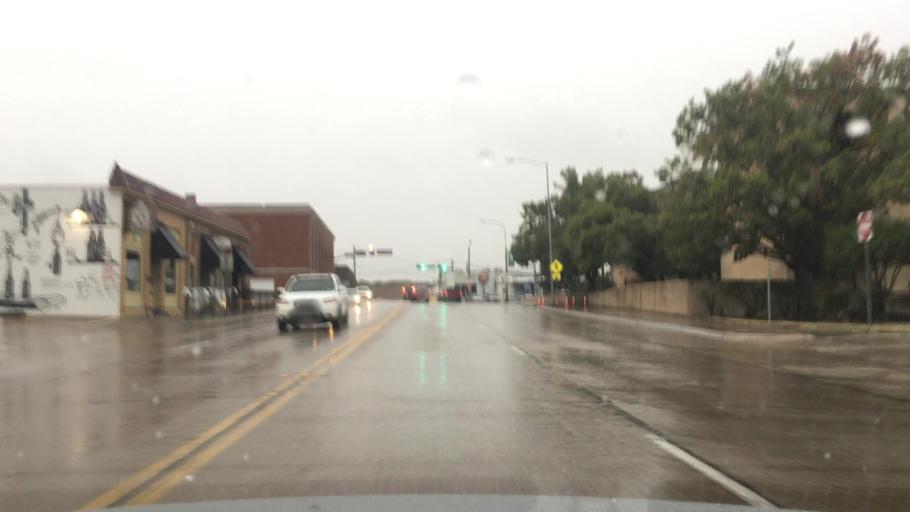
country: US
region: Texas
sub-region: Denton County
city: Denton
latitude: 33.2166
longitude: -97.1312
